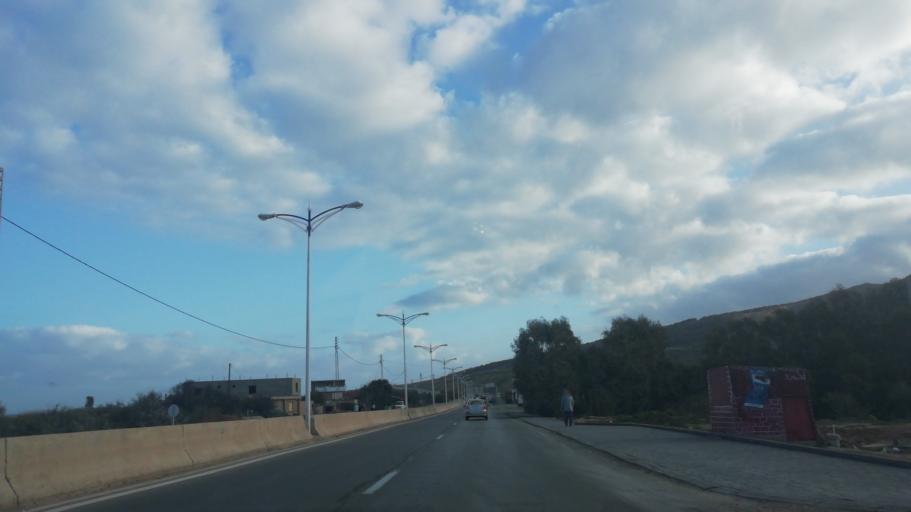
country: DZ
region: Mostaganem
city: Mostaganem
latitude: 36.0302
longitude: 0.1379
